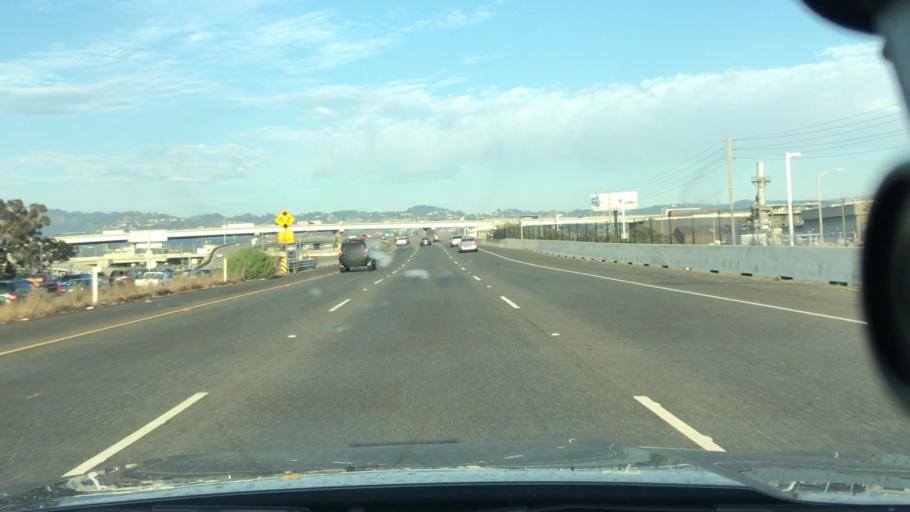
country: US
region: California
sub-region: Alameda County
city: Emeryville
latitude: 37.8261
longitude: -122.2985
